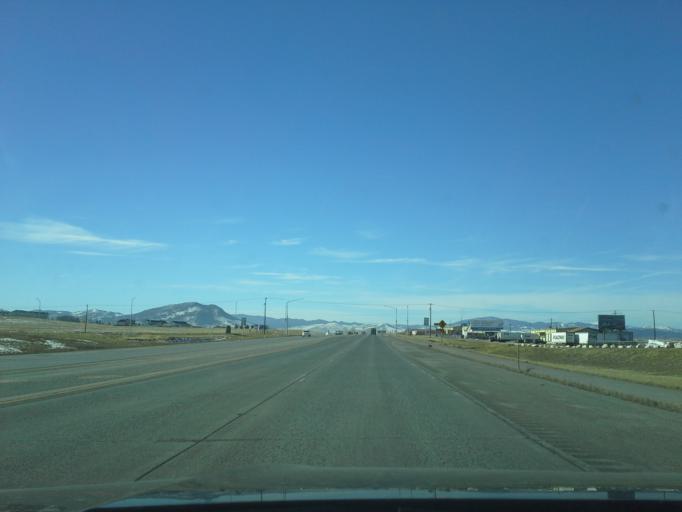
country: US
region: Montana
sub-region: Lewis and Clark County
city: East Helena
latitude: 46.5905
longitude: -111.9533
